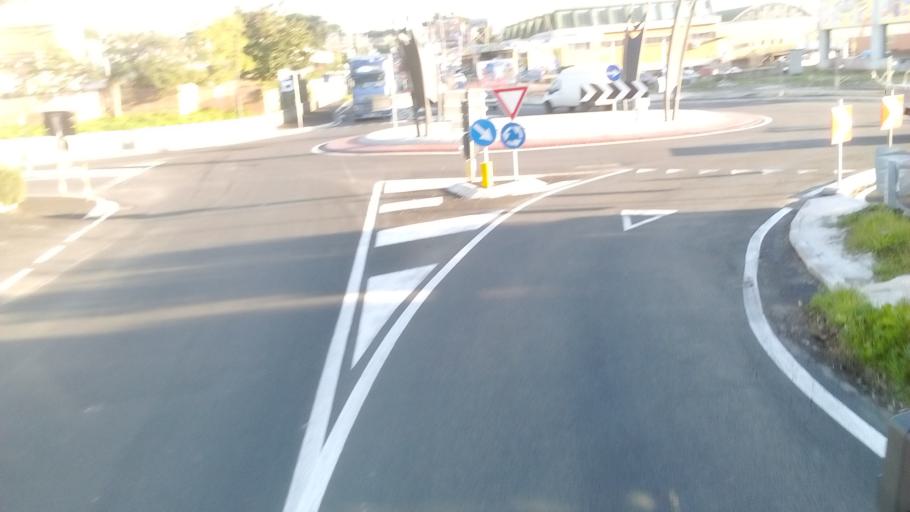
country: IT
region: Latium
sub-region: Citta metropolitana di Roma Capitale
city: Albano Laziale
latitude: 41.7152
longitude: 12.6302
